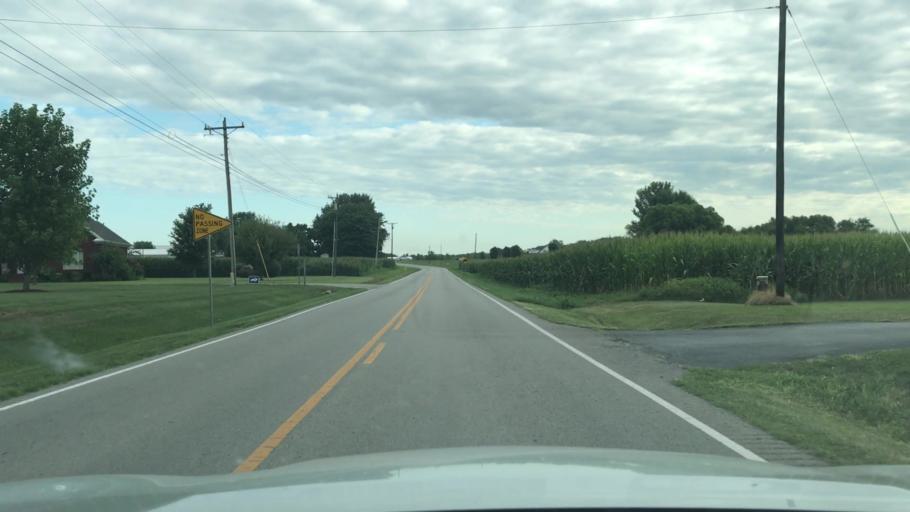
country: US
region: Kentucky
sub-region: Todd County
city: Elkton
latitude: 36.7790
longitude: -87.1641
